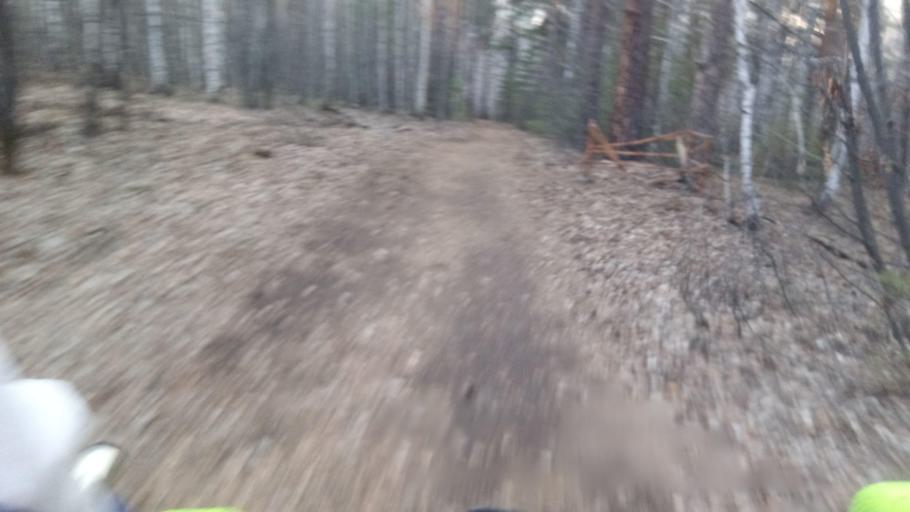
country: RU
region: Chelyabinsk
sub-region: Gorod Chelyabinsk
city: Chelyabinsk
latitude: 55.1655
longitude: 61.3240
